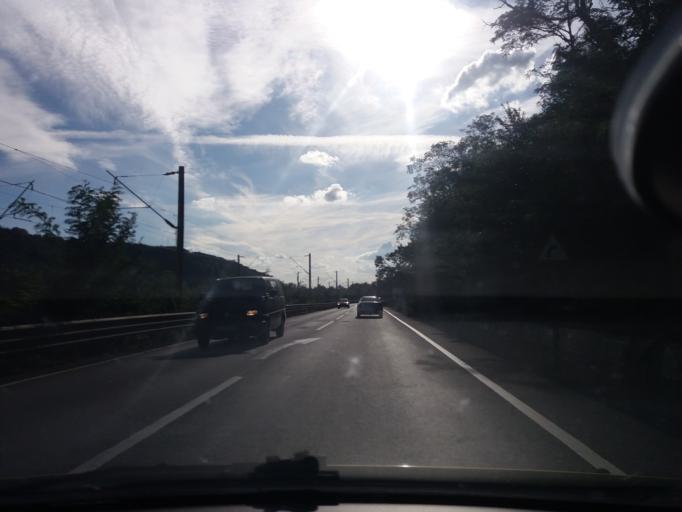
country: RO
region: Arad
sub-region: Oras Lipova
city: Lipova
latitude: 46.1076
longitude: 21.7245
